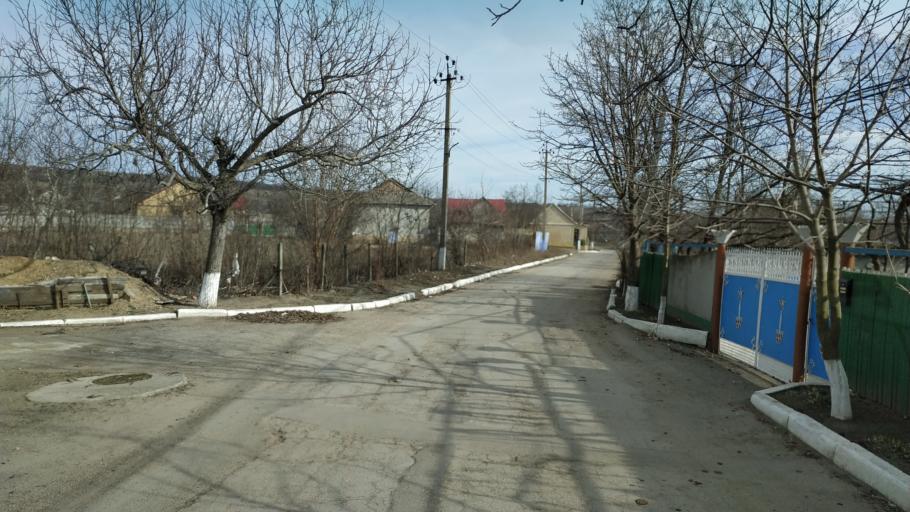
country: RO
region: Iasi
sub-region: Comuna Gorban
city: Gorban
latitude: 46.8788
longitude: 28.1612
